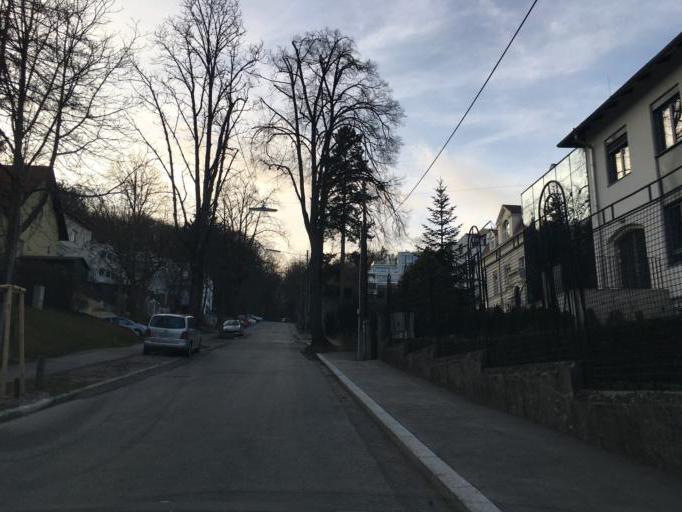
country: AT
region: Vienna
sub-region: Wien Stadt
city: Vienna
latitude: 48.2172
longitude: 16.2871
